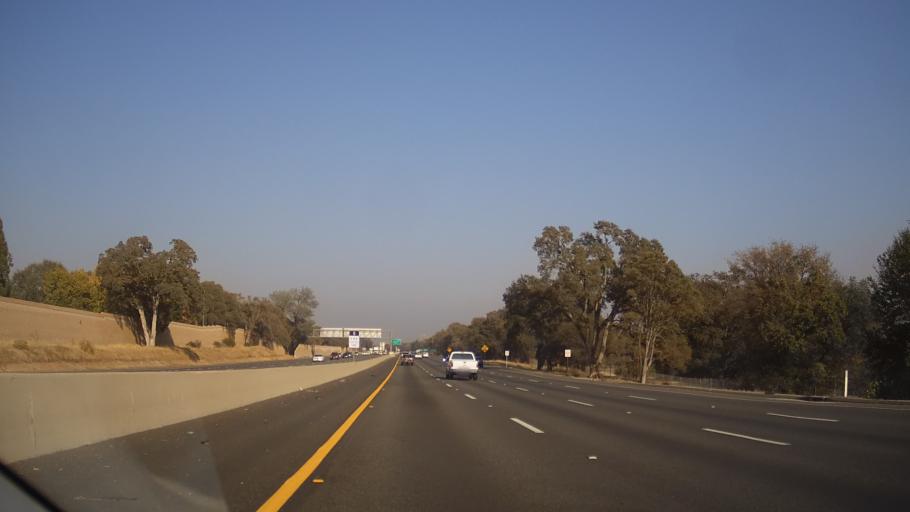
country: US
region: California
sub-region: Placer County
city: Rocklin
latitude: 38.7745
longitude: -121.2413
